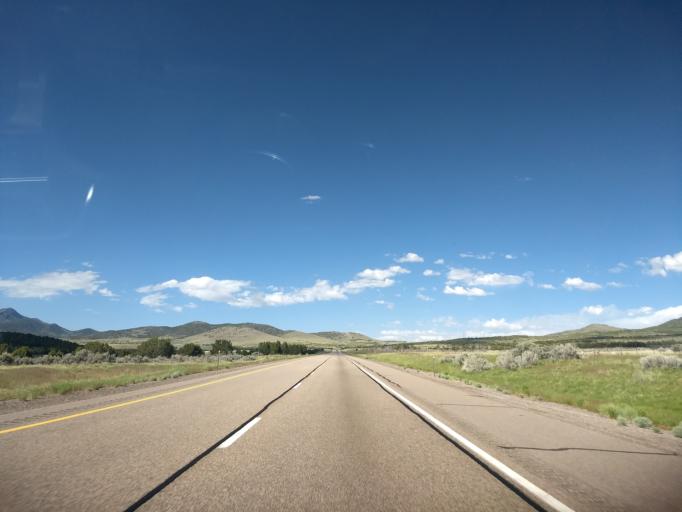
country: US
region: Utah
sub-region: Millard County
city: Fillmore
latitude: 39.1724
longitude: -112.2113
